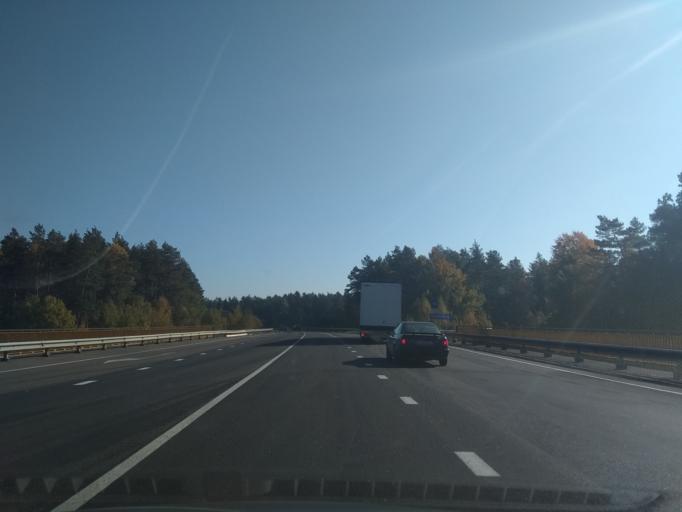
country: BY
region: Brest
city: Baranovichi
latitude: 53.0482
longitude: 25.8441
